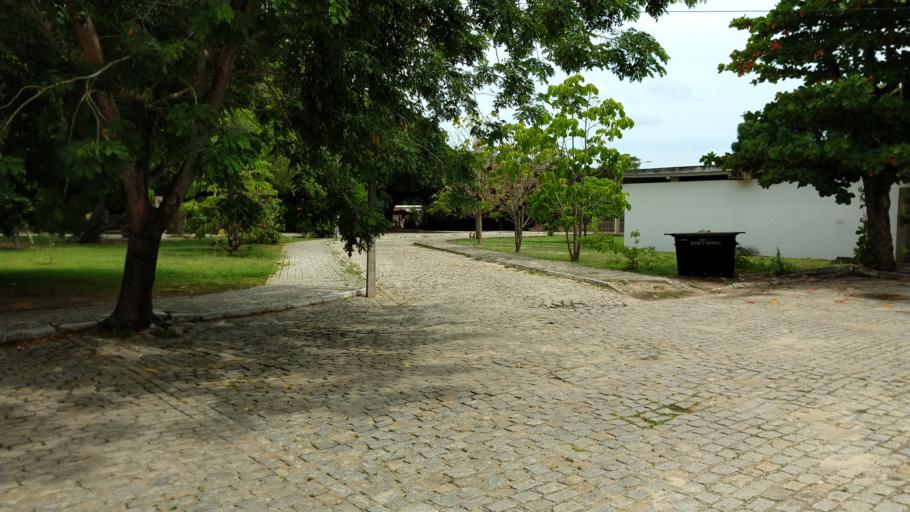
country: BR
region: Ceara
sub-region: Fortaleza
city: Fortaleza
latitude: -3.7468
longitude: -38.5750
